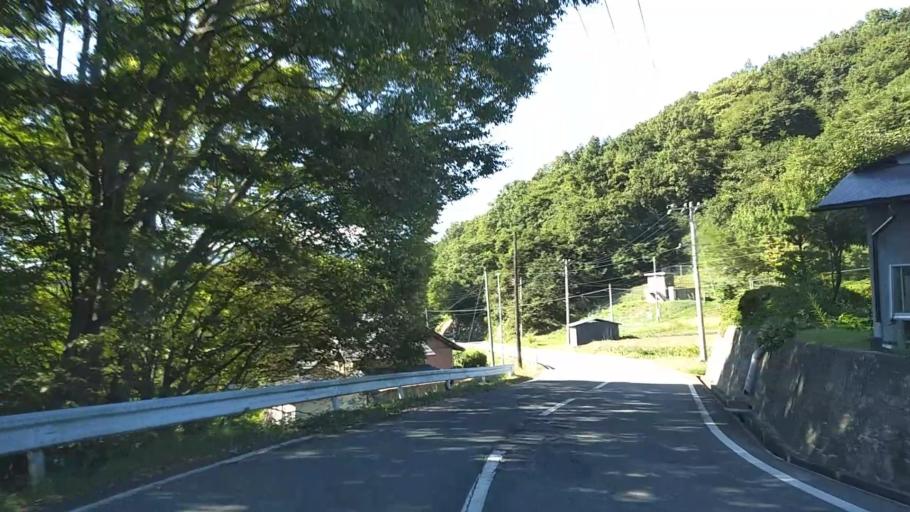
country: JP
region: Nagano
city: Nagano-shi
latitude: 36.6056
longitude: 138.0927
